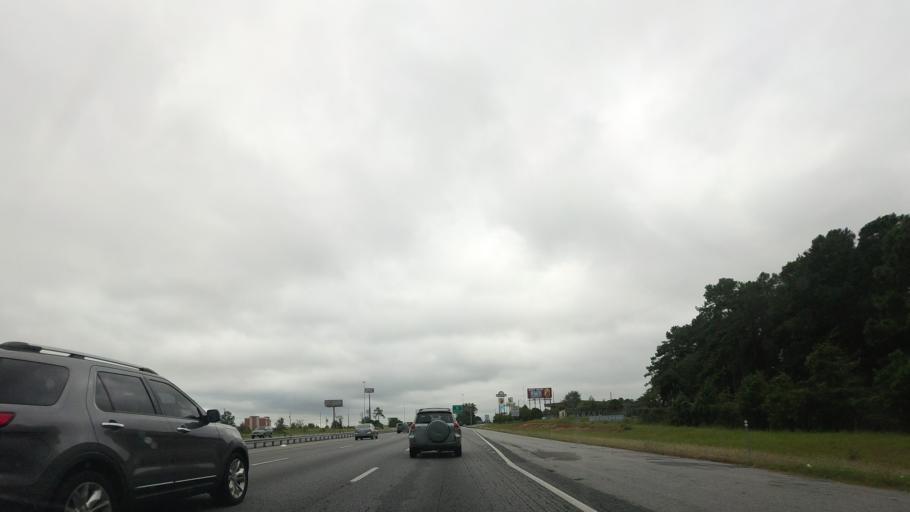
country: US
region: Georgia
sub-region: Lowndes County
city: Remerton
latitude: 30.8503
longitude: -83.3328
